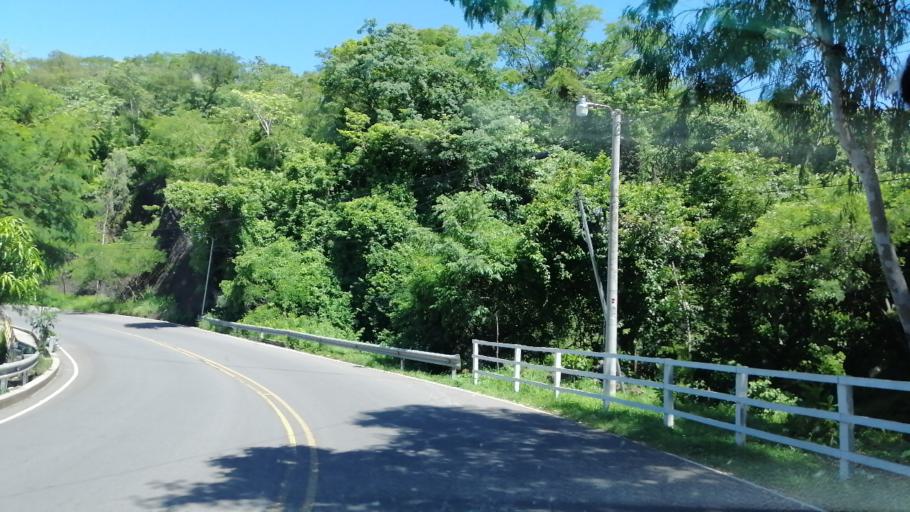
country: SV
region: Morazan
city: Cacaopera
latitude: 13.8086
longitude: -88.1610
